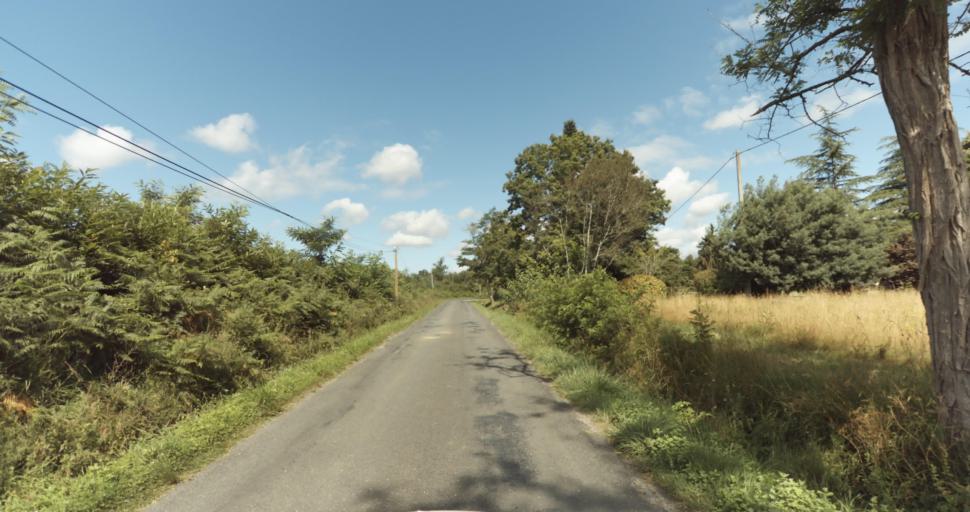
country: FR
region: Aquitaine
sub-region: Departement de la Gironde
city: Bazas
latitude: 44.4519
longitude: -0.2135
